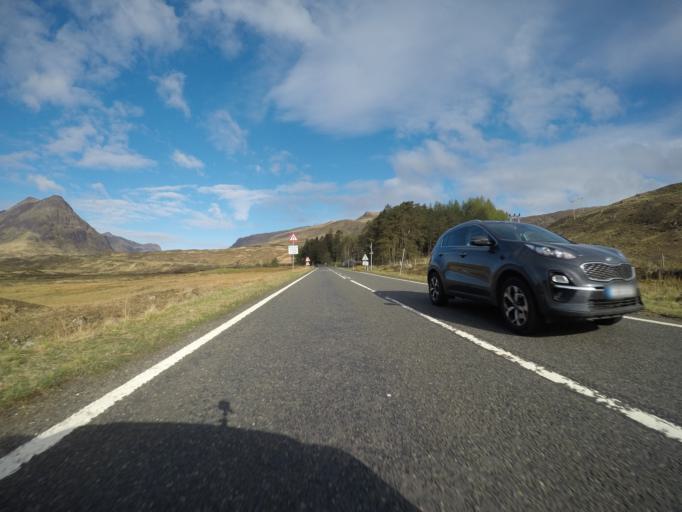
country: GB
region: Scotland
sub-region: Highland
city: Spean Bridge
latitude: 56.6640
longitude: -4.9005
